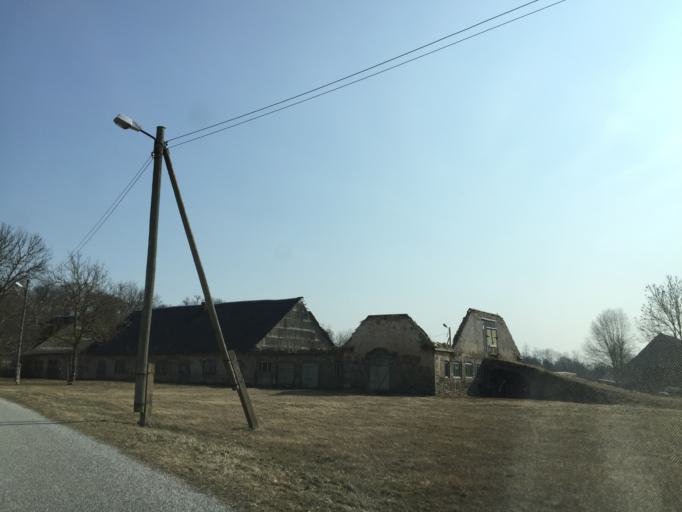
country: EE
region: Saare
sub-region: Kuressaare linn
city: Kuressaare
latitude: 58.3706
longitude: 22.6818
